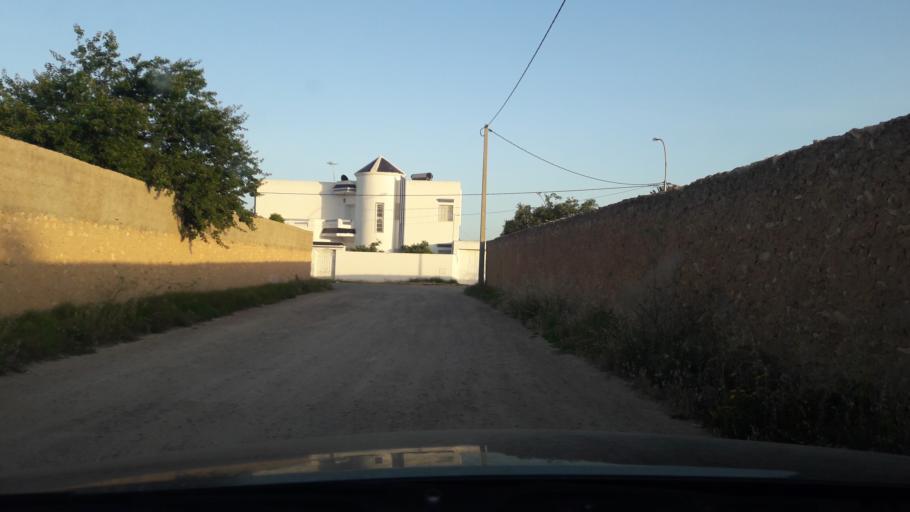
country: TN
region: Safaqis
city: Al Qarmadah
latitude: 34.7913
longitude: 10.7532
